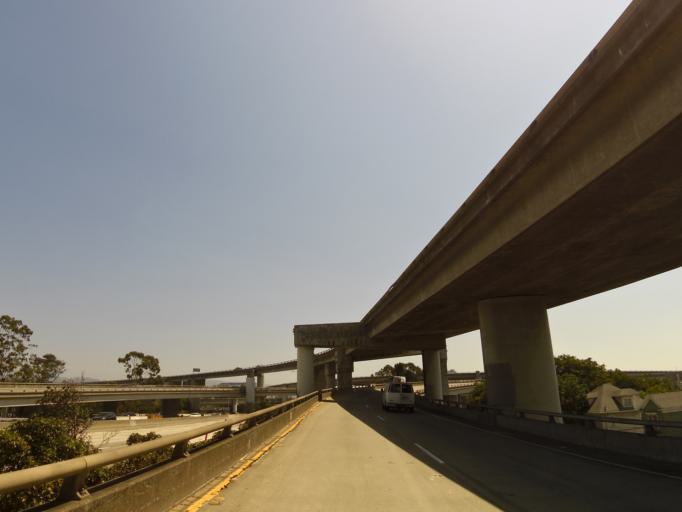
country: US
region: California
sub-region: Alameda County
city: Emeryville
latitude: 37.8248
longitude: -122.2712
